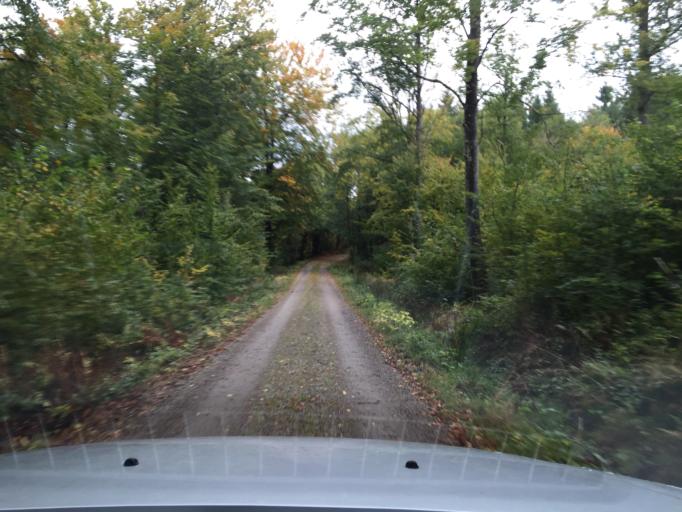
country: SE
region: Skane
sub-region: Hassleholms Kommun
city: Tormestorp
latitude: 56.0636
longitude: 13.7539
